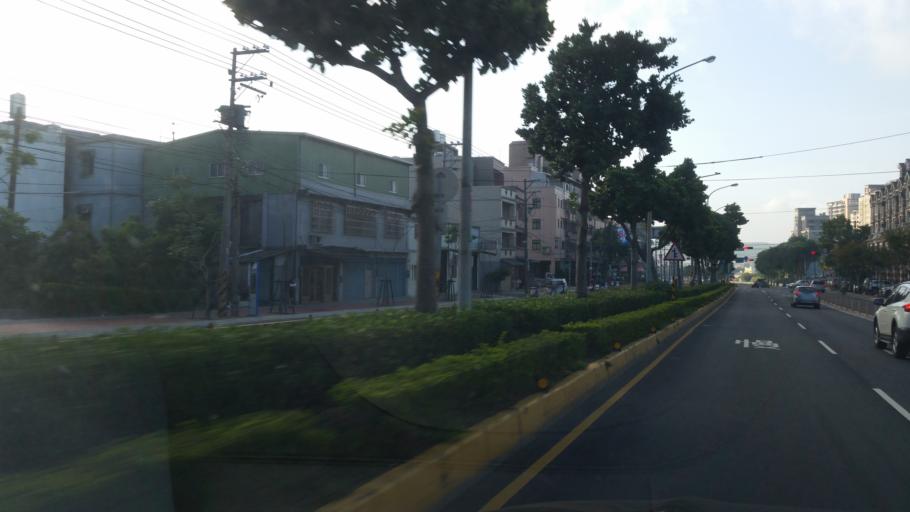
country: TW
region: Taiwan
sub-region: Taoyuan
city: Taoyuan
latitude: 25.0081
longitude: 121.3448
